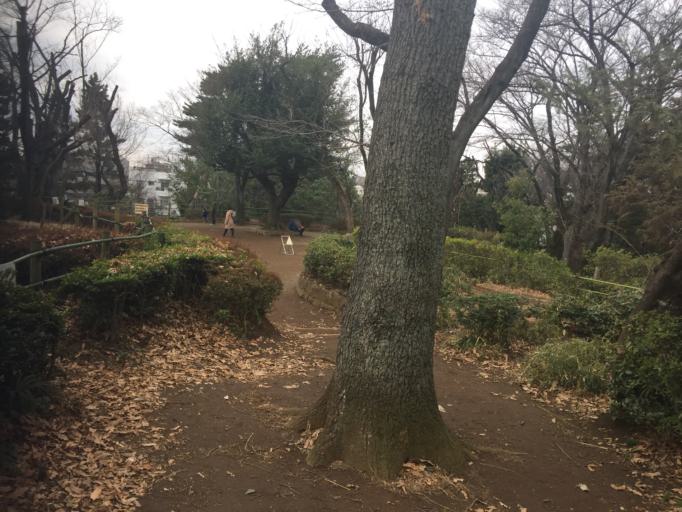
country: JP
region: Tokyo
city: Tokyo
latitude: 35.6576
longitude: 139.6561
